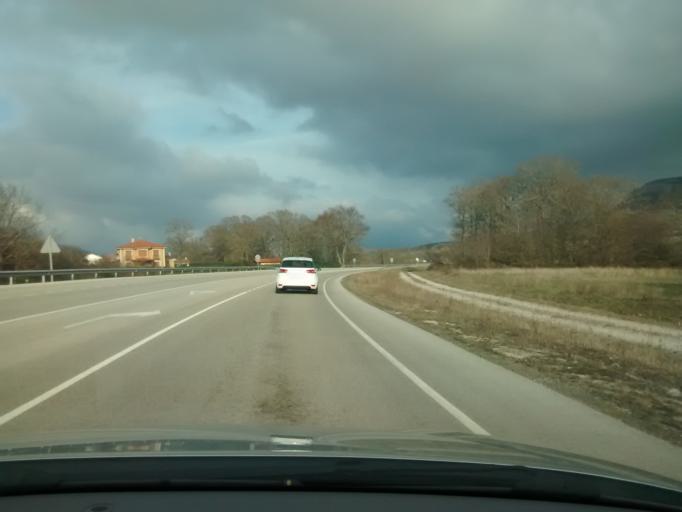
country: ES
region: Castille and Leon
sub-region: Provincia de Burgos
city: Espinosa de los Monteros
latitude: 43.0800
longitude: -3.4576
